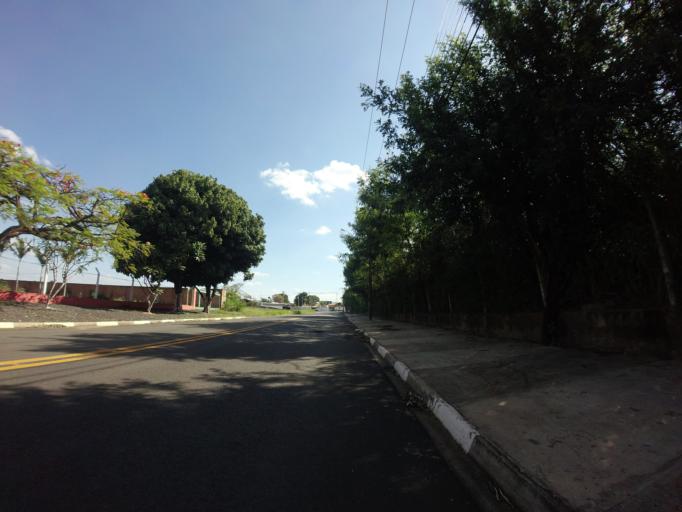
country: BR
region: Sao Paulo
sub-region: Piracicaba
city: Piracicaba
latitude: -22.7434
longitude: -47.5923
